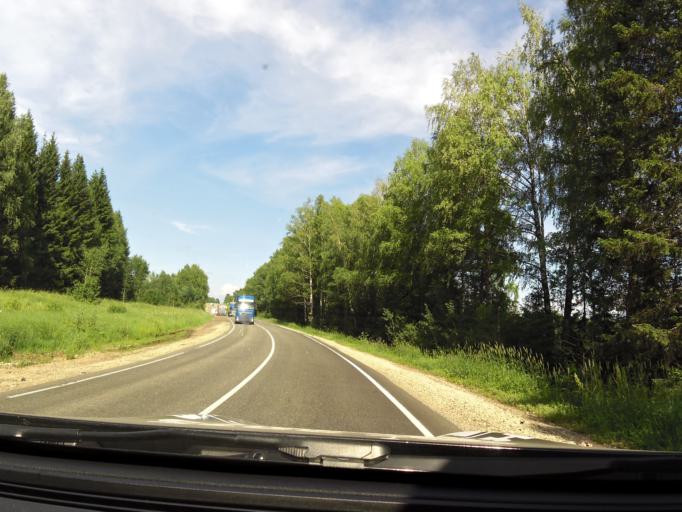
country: RU
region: Kirov
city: Belaya Kholunitsa
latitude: 58.8417
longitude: 50.6957
